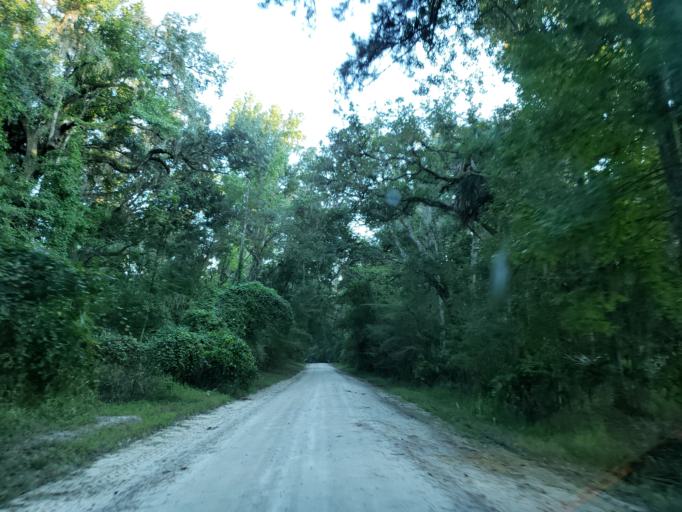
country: US
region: Florida
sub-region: Alachua County
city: Gainesville
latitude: 29.4864
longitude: -82.2770
